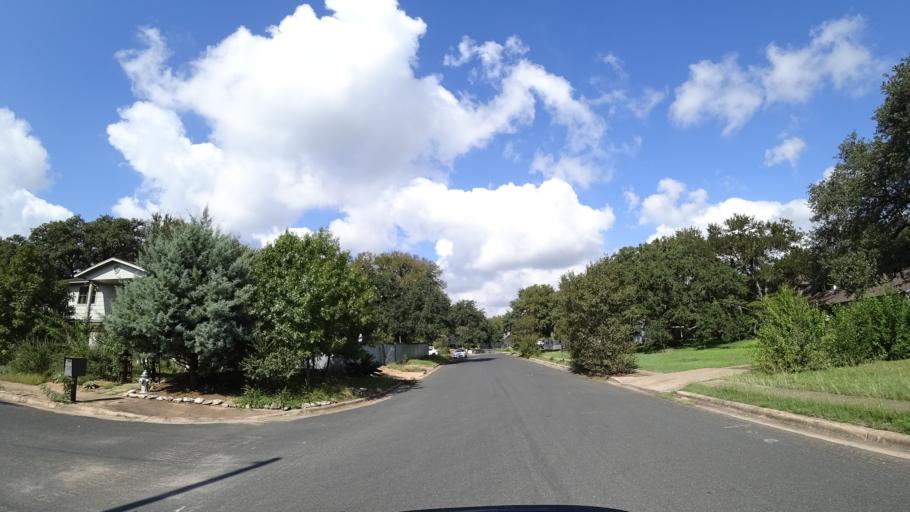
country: US
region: Texas
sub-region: Travis County
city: Shady Hollow
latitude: 30.2026
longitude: -97.8109
